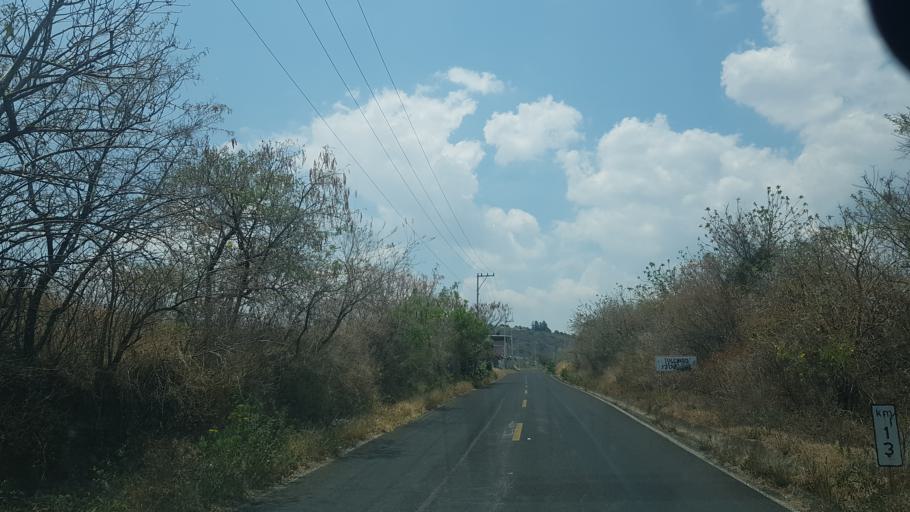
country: MX
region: Puebla
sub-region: Atzitzihuacan
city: Santiago Atzitzihuacan
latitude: 18.8326
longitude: -98.5909
